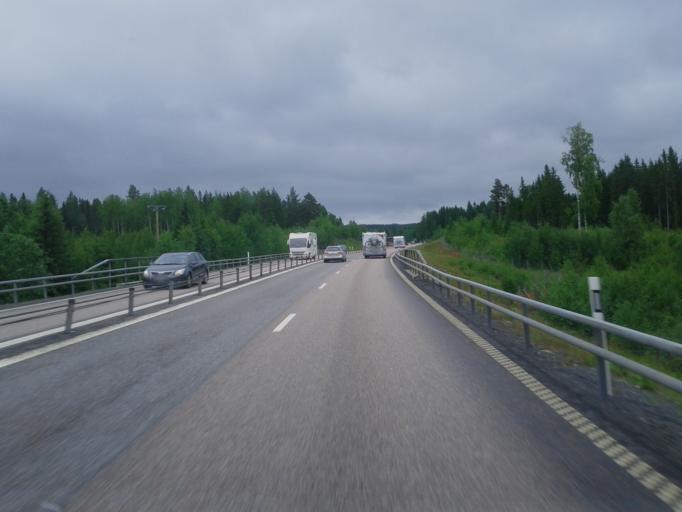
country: SE
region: Vaesternorrland
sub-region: Kramfors Kommun
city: Nordingra
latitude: 62.9142
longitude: 18.0942
